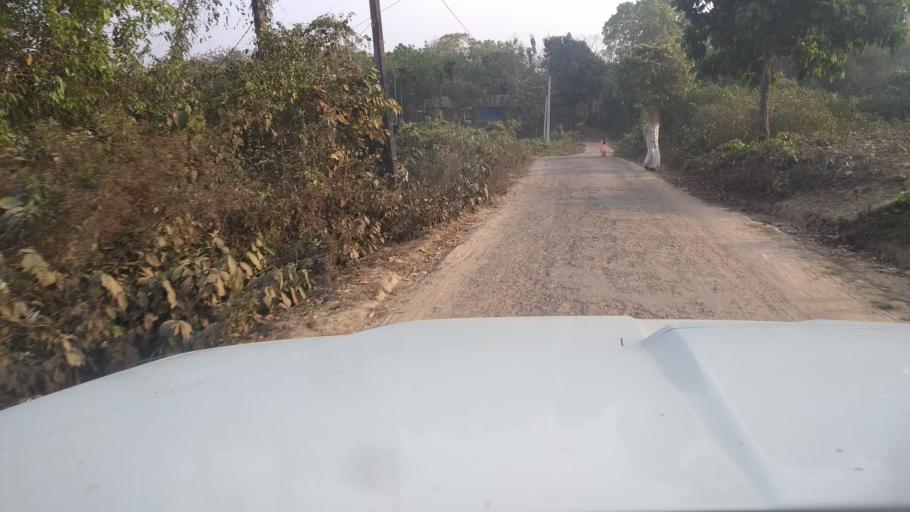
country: IN
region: Tripura
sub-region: West Tripura
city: Sonamura
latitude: 23.3267
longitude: 91.3024
